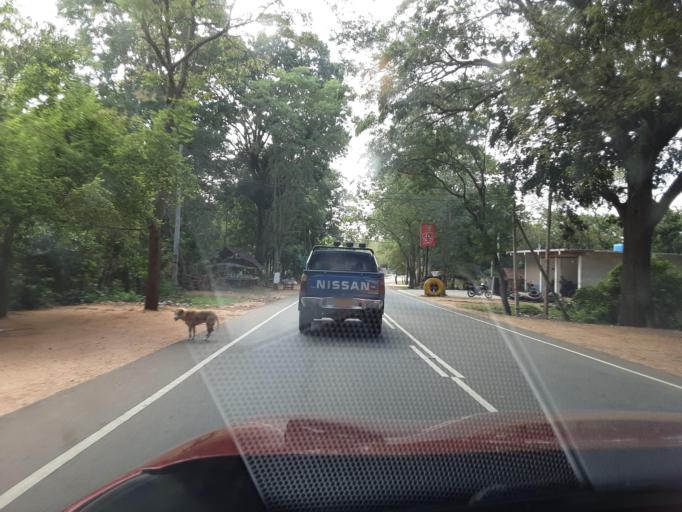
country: LK
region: Uva
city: Haputale
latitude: 6.3592
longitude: 81.1833
